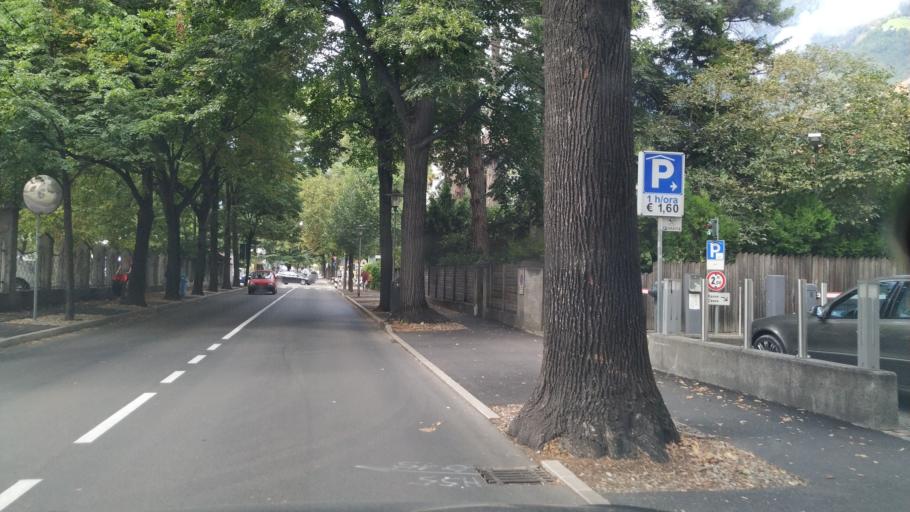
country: IT
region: Trentino-Alto Adige
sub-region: Bolzano
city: Merano
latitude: 46.6755
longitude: 11.1545
